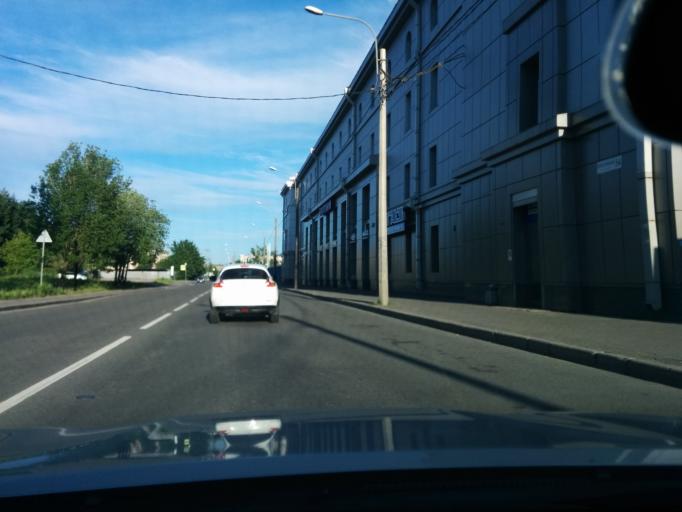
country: RU
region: Leningrad
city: Finlyandskiy
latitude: 59.9766
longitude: 30.3685
